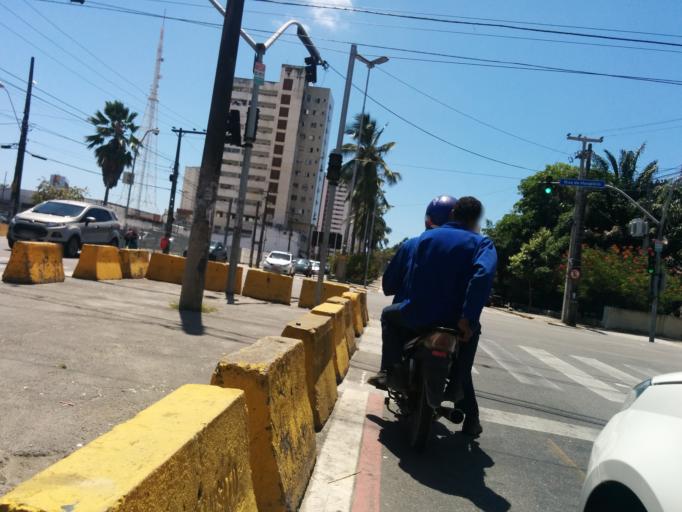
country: BR
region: Pernambuco
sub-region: Recife
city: Recife
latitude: -8.0539
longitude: -34.8818
